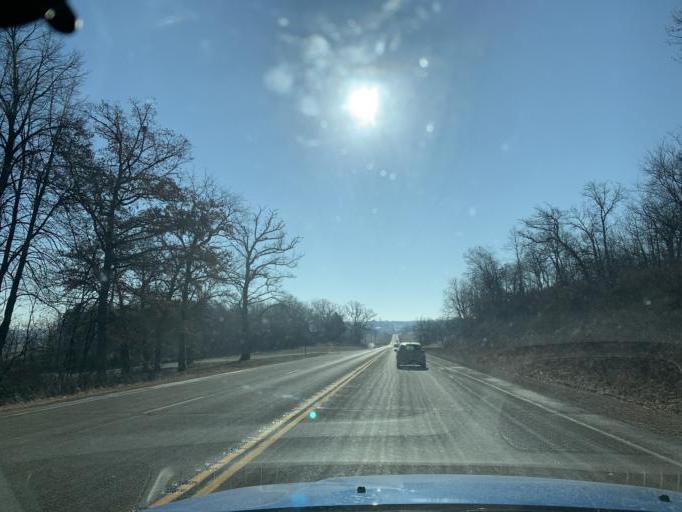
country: US
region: Wisconsin
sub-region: Green County
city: Monticello
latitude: 42.7298
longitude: -89.5987
